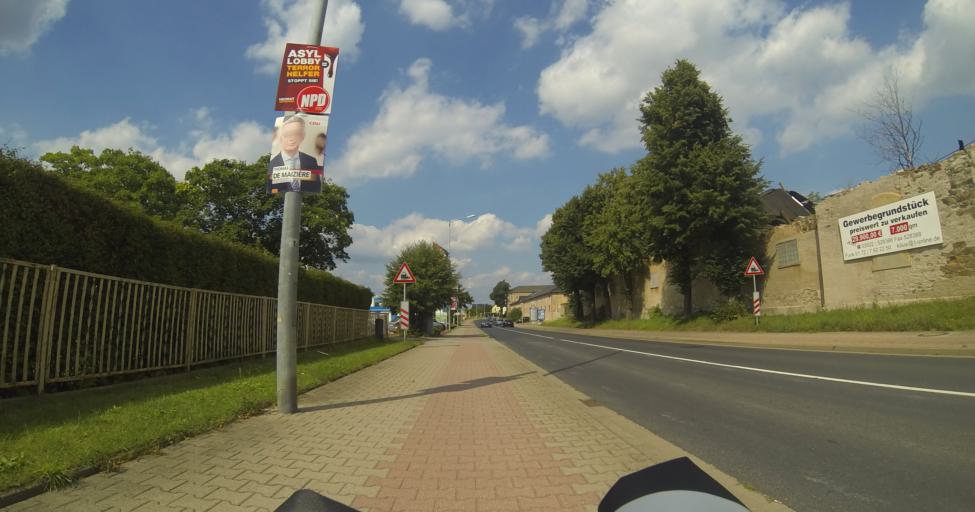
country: DE
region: Saxony
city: Grossenhain
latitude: 51.2970
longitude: 13.5342
